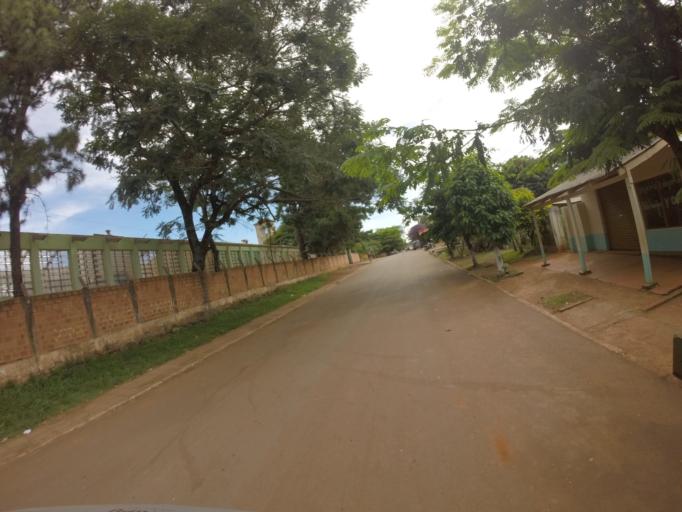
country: PY
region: Alto Parana
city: Ciudad del Este
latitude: -25.4338
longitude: -54.6409
